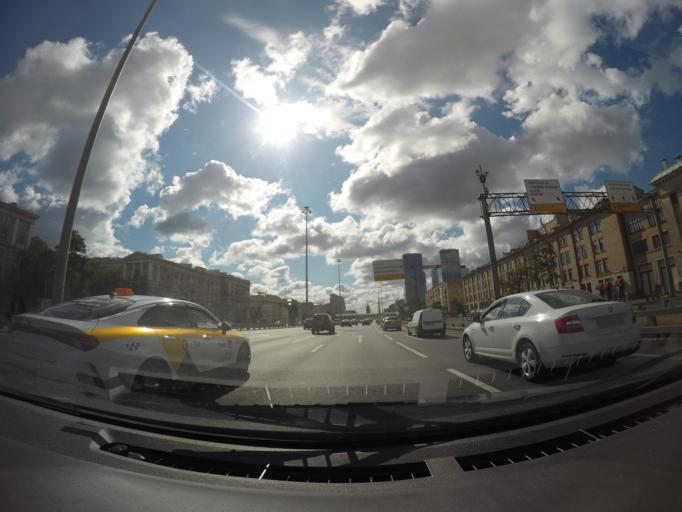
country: RU
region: Moscow
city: Sokol
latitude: 55.8004
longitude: 37.5314
